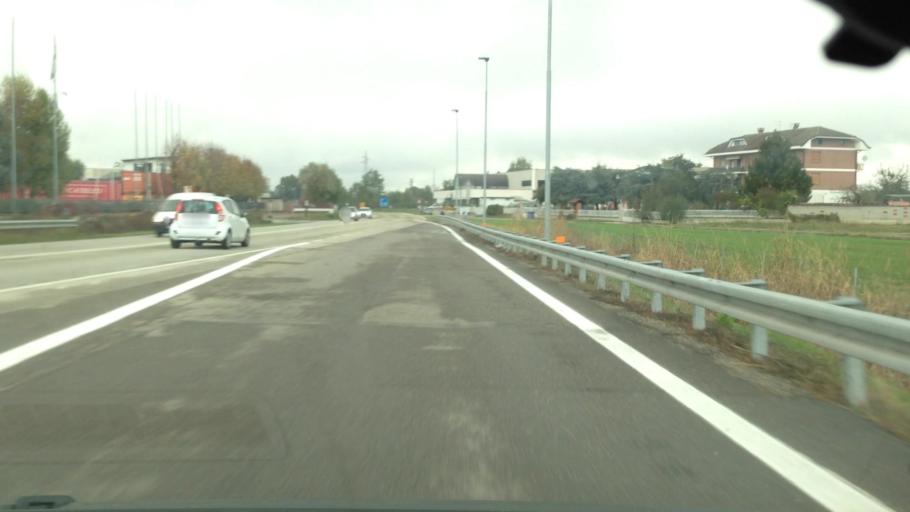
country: IT
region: Piedmont
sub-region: Provincia di Asti
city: Villanova d'Asti
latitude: 44.9565
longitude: 7.9147
